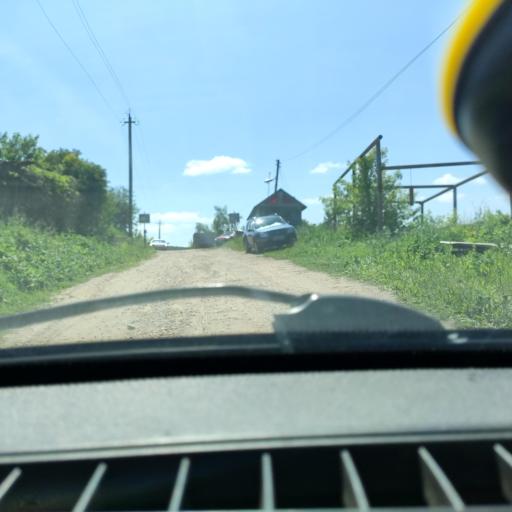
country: RU
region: Samara
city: Zhigulevsk
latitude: 53.3749
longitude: 49.5094
